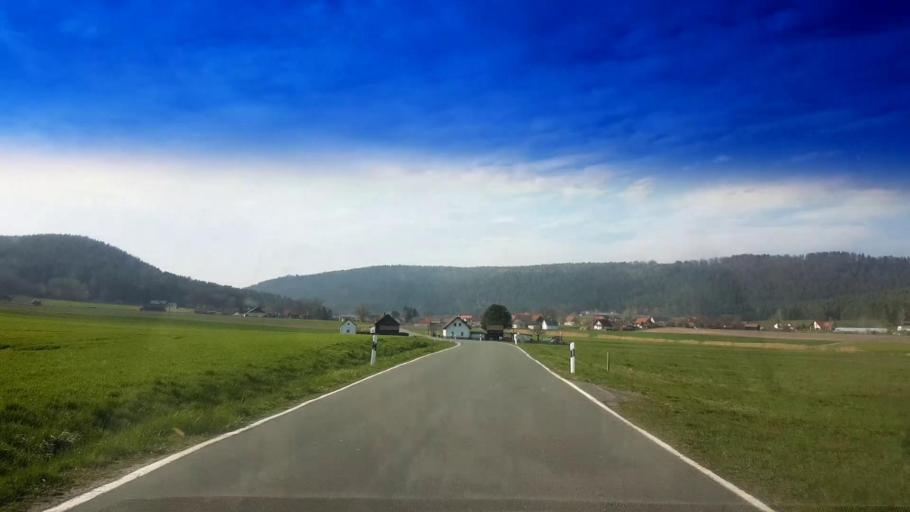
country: DE
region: Bavaria
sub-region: Upper Franconia
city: Trebgast
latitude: 50.0517
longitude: 11.5182
